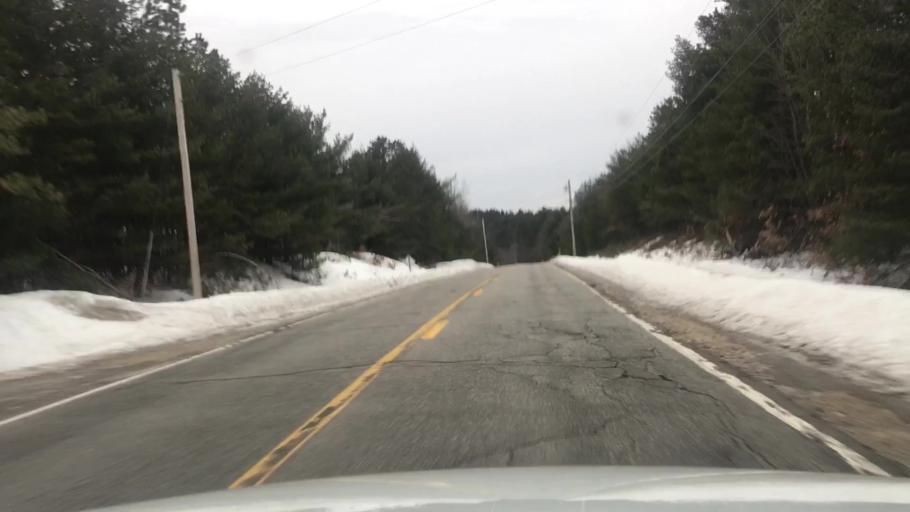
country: US
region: Maine
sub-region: York County
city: Newfield
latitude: 43.5989
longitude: -70.8827
